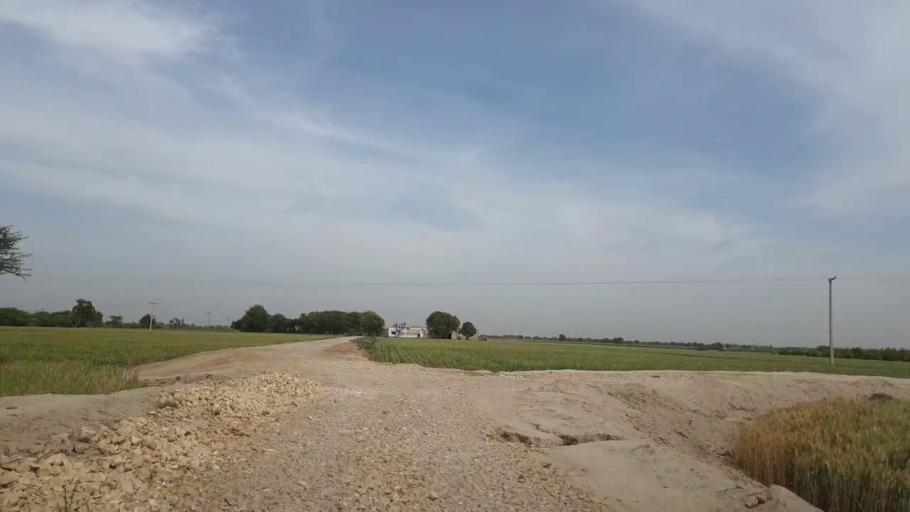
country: PK
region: Sindh
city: Kunri
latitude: 25.1828
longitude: 69.5887
